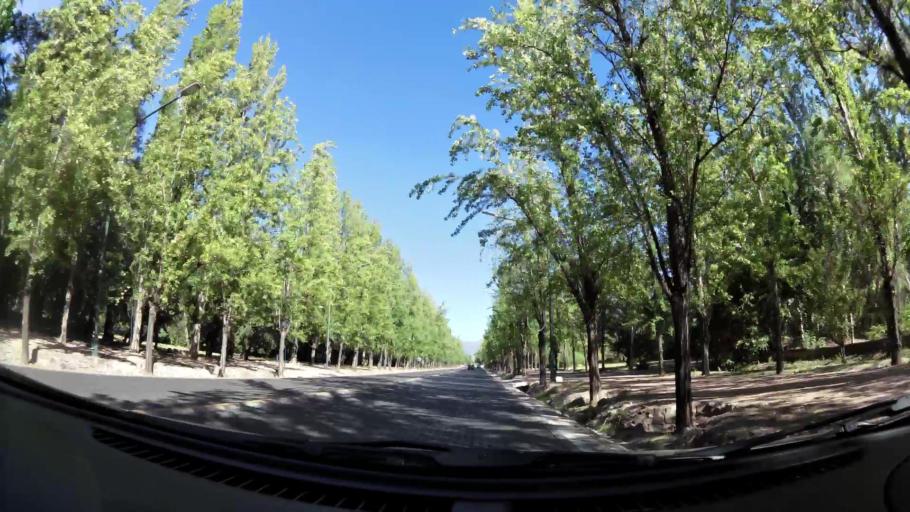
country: AR
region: Mendoza
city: Mendoza
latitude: -32.8850
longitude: -68.8698
